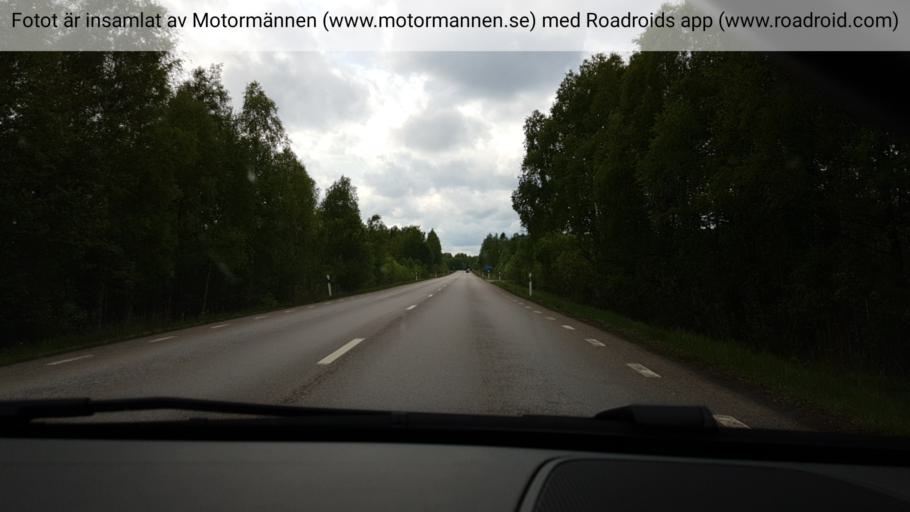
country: SE
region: Uppsala
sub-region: Osthammars Kommun
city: Osterbybruk
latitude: 60.1949
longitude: 17.8365
